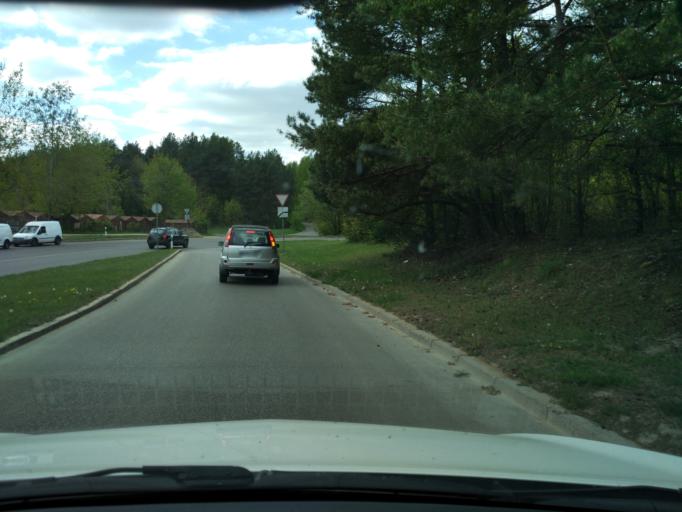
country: LT
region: Vilnius County
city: Rasos
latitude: 54.6930
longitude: 25.3430
